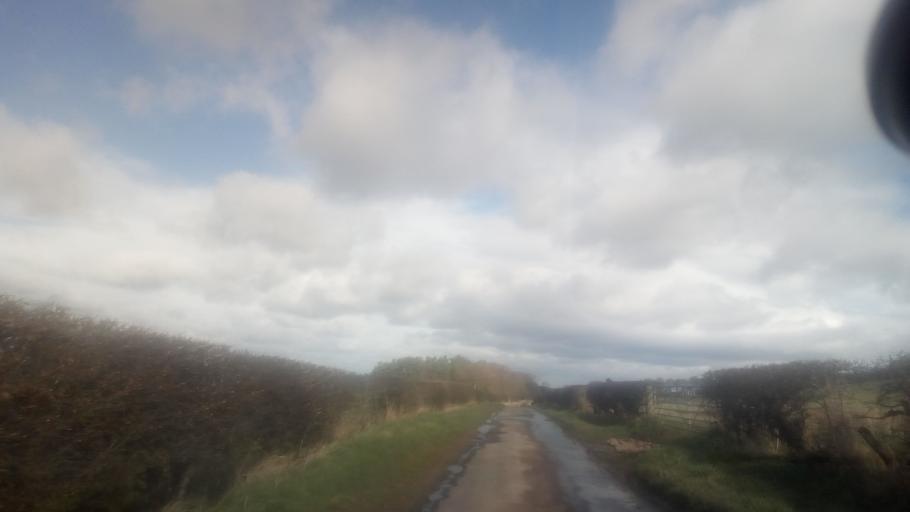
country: GB
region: Scotland
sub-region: The Scottish Borders
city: Jedburgh
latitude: 55.4795
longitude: -2.6084
